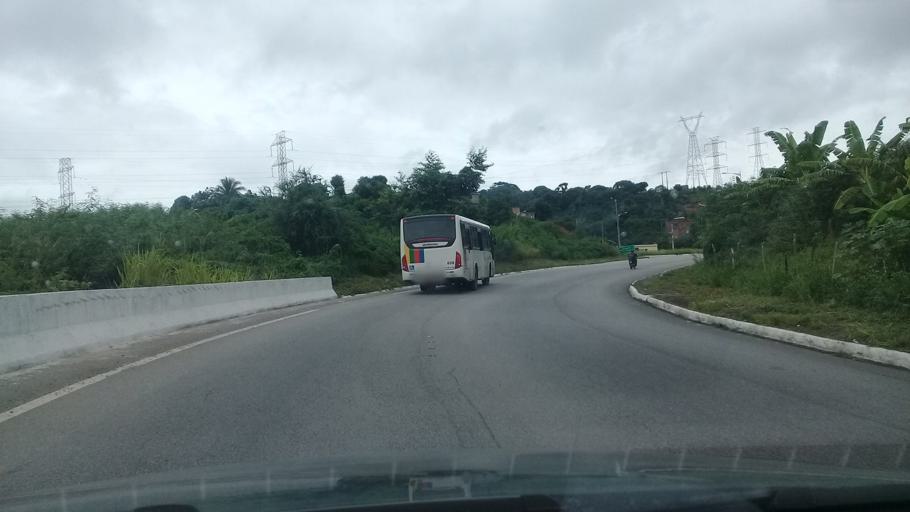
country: BR
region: Pernambuco
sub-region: Jaboatao Dos Guararapes
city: Jaboatao dos Guararapes
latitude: -8.0808
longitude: -34.9909
